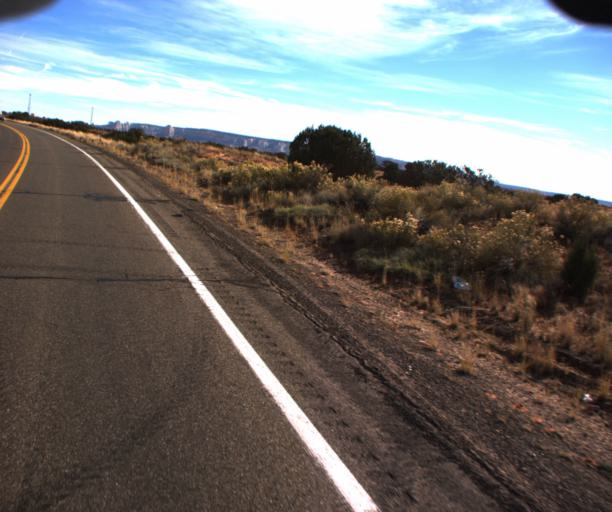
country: US
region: Arizona
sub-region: Coconino County
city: Kaibito
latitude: 36.5759
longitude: -111.1192
